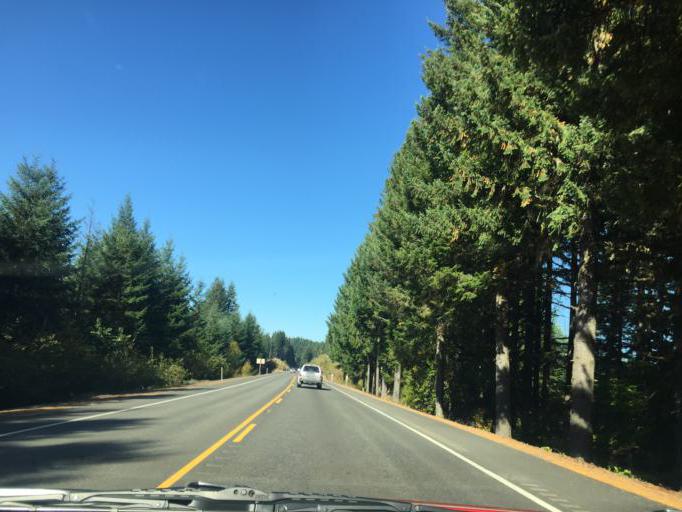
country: US
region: Oregon
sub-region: Columbia County
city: Vernonia
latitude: 45.7363
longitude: -123.2593
